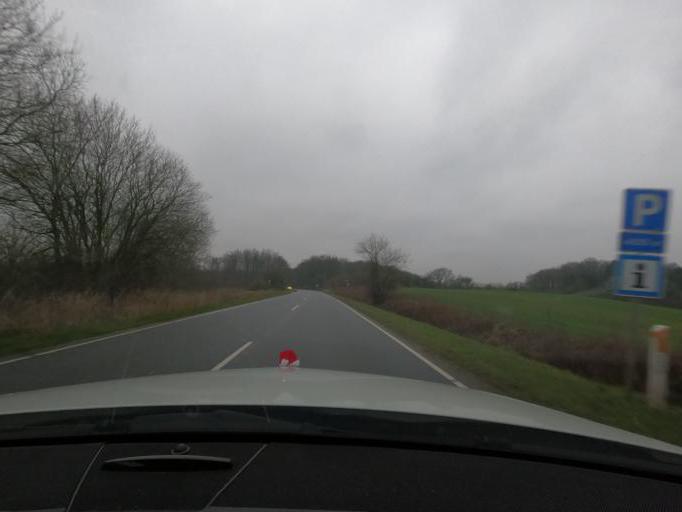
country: DK
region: South Denmark
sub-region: Haderslev Kommune
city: Haderslev
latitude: 55.1945
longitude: 9.4184
